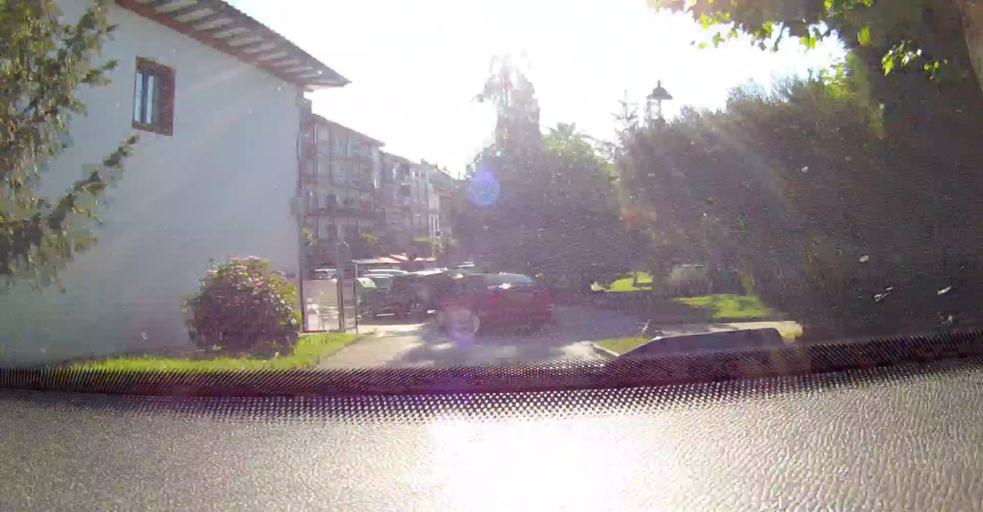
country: ES
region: Asturias
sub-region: Province of Asturias
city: Villaviciosa
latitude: 43.4812
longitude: -5.4320
